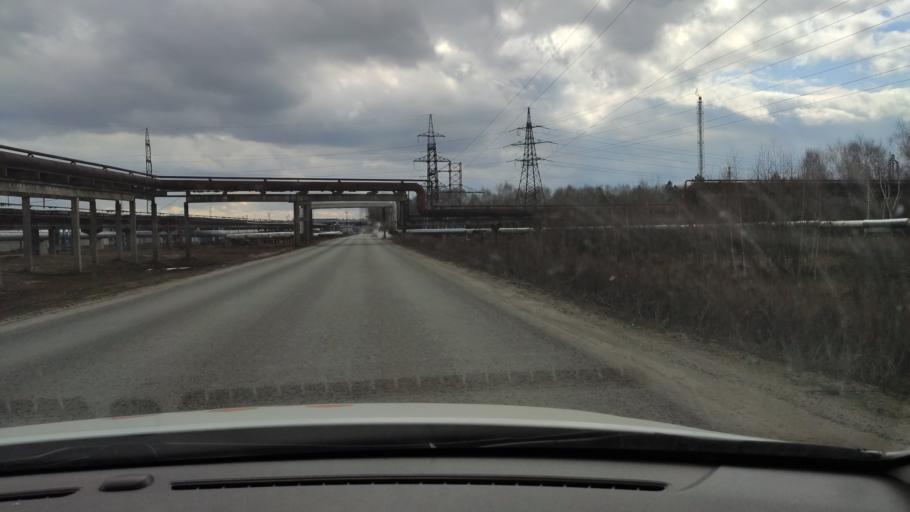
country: RU
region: Tatarstan
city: Staroye Arakchino
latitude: 55.8688
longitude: 48.9733
